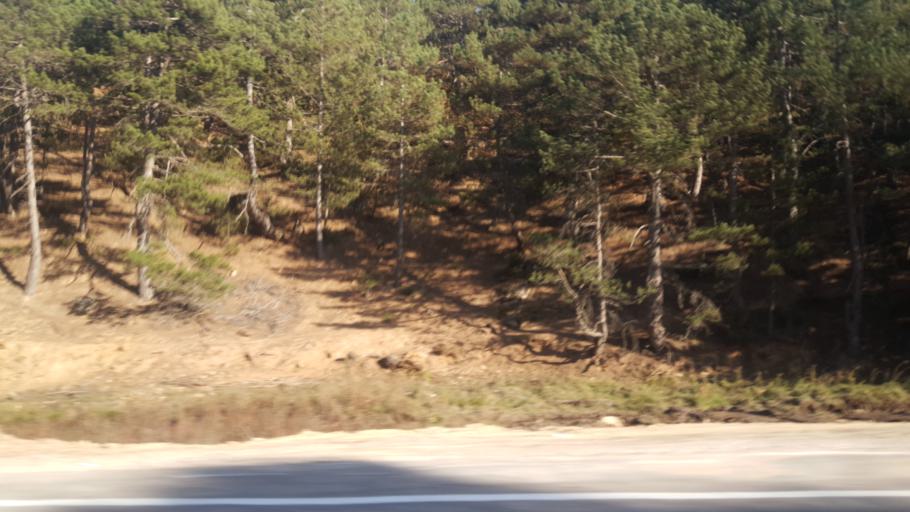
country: TR
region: Afyonkarahisar
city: Ihsaniye
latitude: 39.1050
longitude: 30.5814
